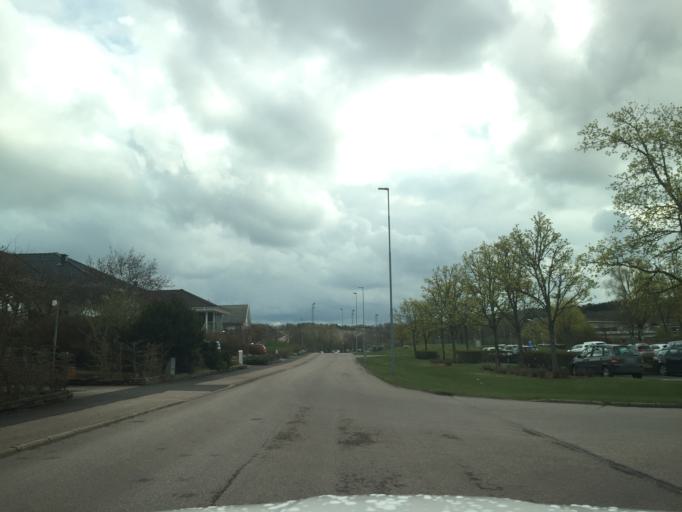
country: SE
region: Vaestra Goetaland
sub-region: Kungalvs Kommun
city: Kungalv
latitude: 57.8907
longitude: 11.9632
